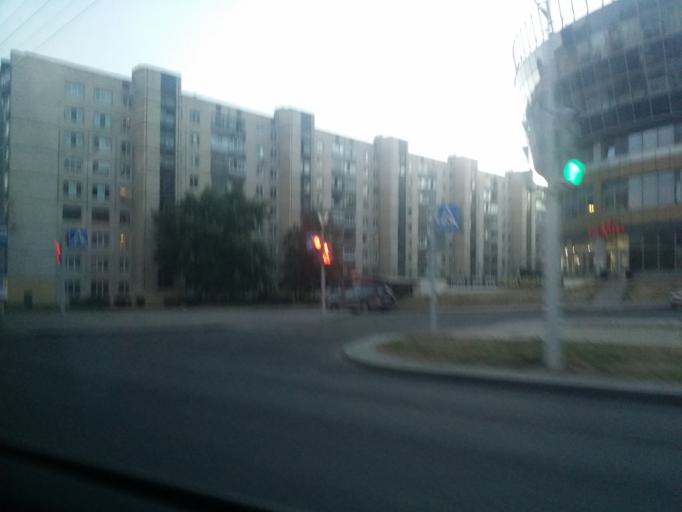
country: BY
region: Minsk
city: Minsk
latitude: 53.9279
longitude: 27.5850
